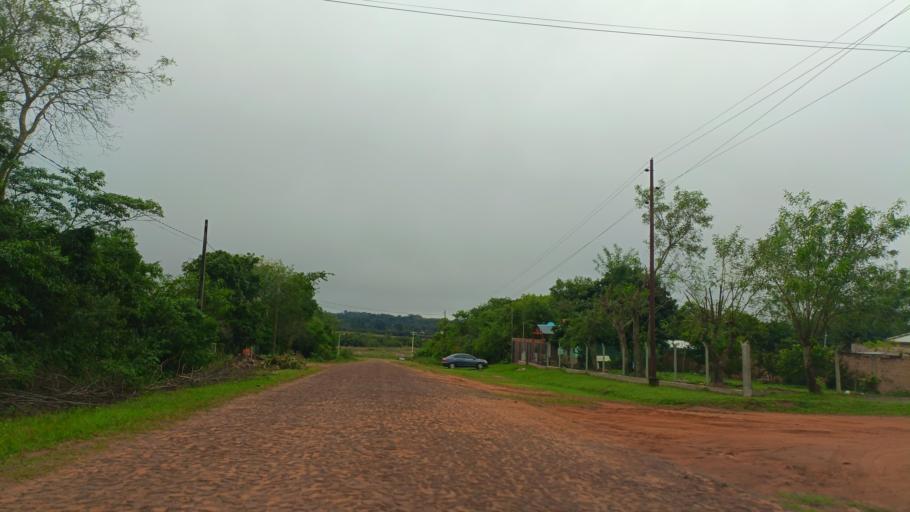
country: PY
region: Misiones
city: Santa Maria
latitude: -26.8727
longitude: -57.0085
